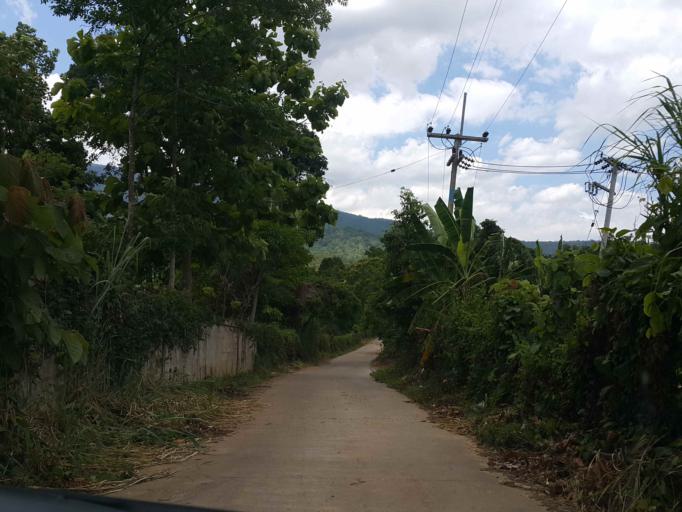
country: TH
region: Chiang Mai
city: Hang Dong
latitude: 18.7757
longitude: 98.8525
